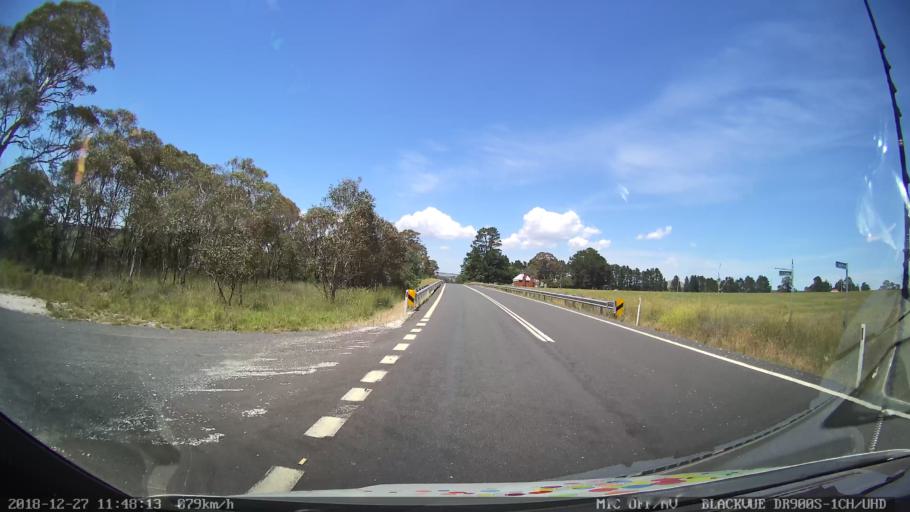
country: AU
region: New South Wales
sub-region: Bathurst Regional
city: Perthville
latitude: -33.6037
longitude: 149.4370
